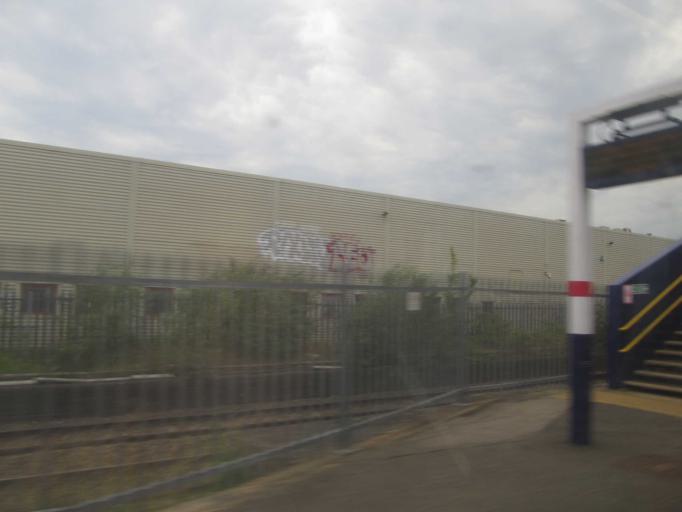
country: GB
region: England
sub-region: Greater London
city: Hendon
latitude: 51.5788
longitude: -0.2385
